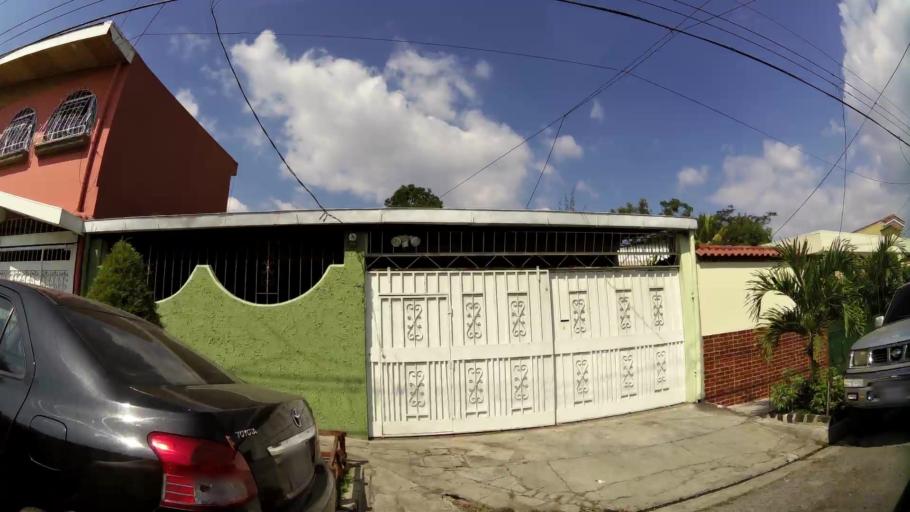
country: SV
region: San Salvador
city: Mejicanos
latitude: 13.7244
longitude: -89.2185
